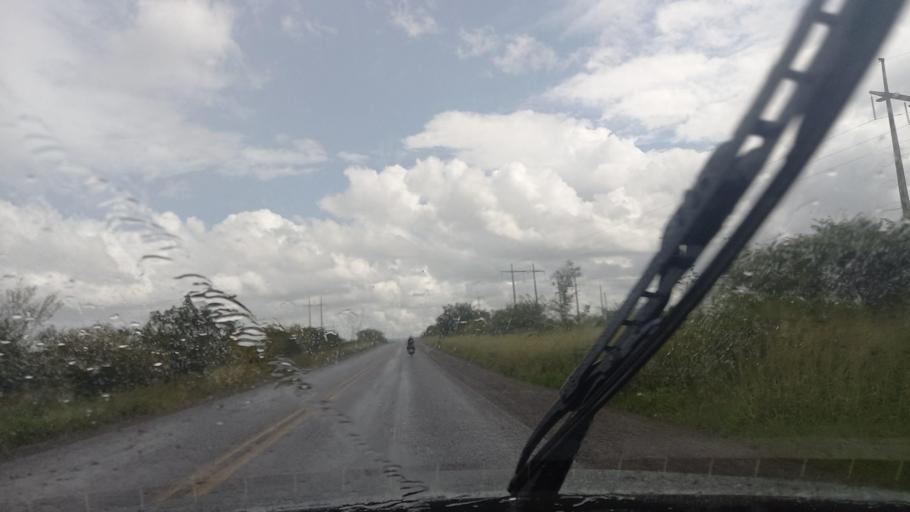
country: BR
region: Pernambuco
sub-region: Cachoeirinha
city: Cachoeirinha
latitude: -8.5699
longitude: -36.2816
